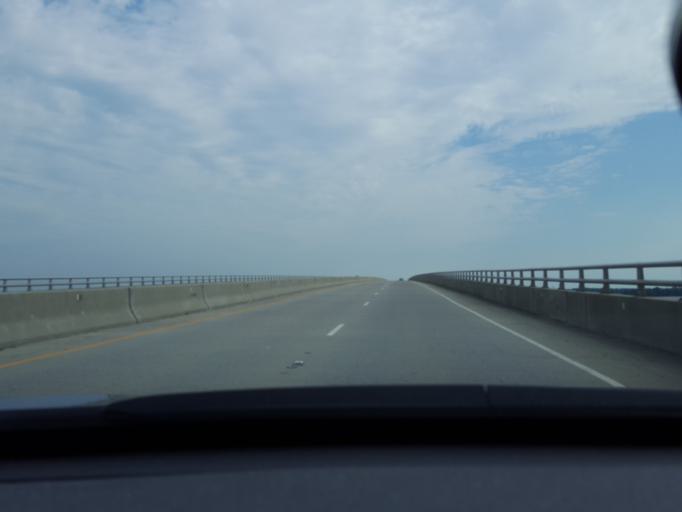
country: US
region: North Carolina
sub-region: Chowan County
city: Edenton
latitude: 36.0450
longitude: -76.7008
